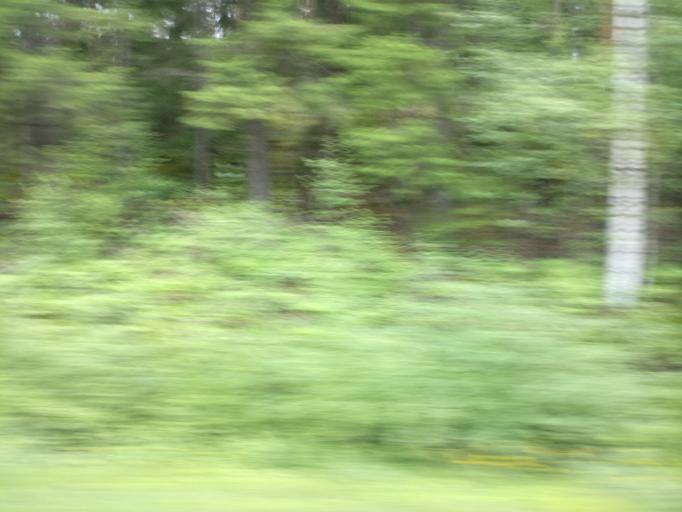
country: FI
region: Northern Savo
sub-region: Varkaus
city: Kangaslampi
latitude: 62.1860
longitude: 28.1009
